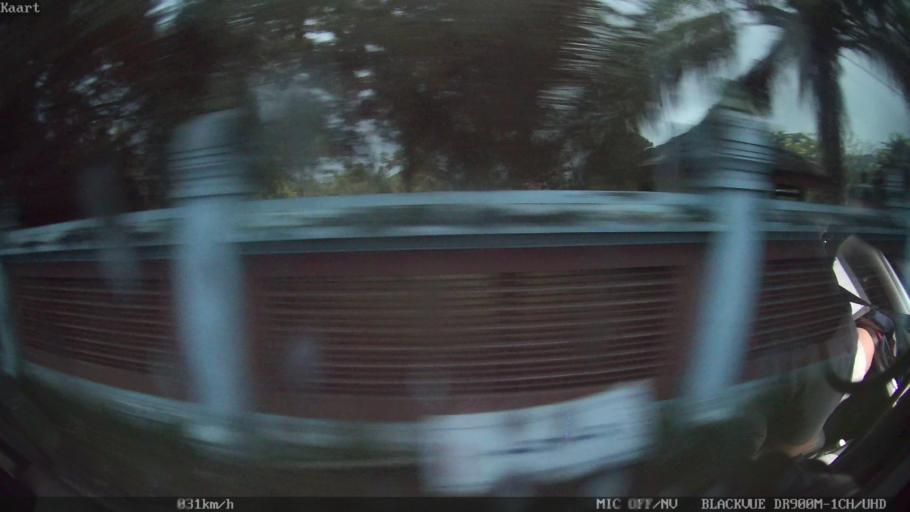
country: ID
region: Bali
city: Banjar Batur
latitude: -8.5998
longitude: 115.2191
